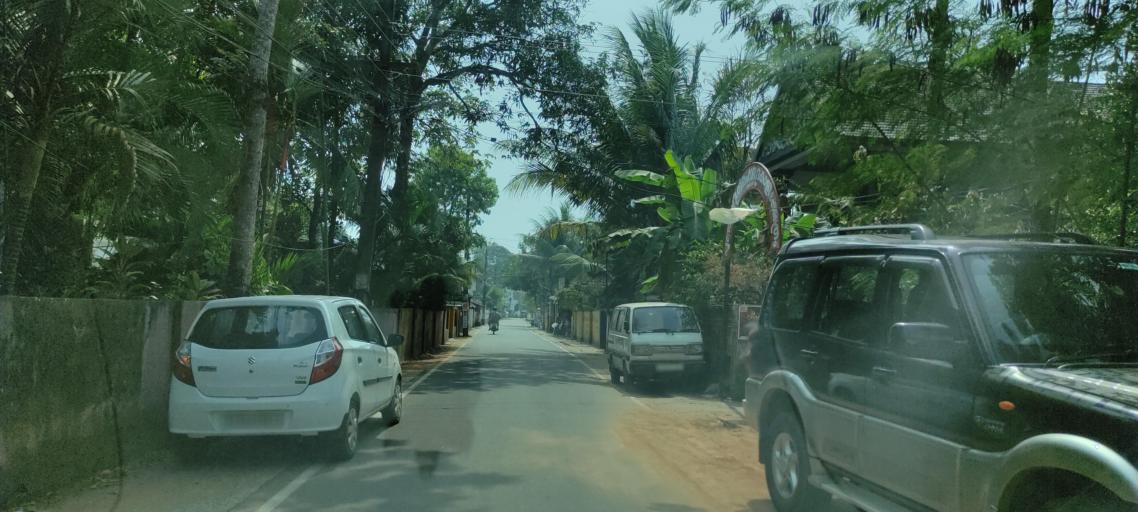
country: IN
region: Kerala
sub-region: Alappuzha
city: Alleppey
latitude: 9.5068
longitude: 76.3340
